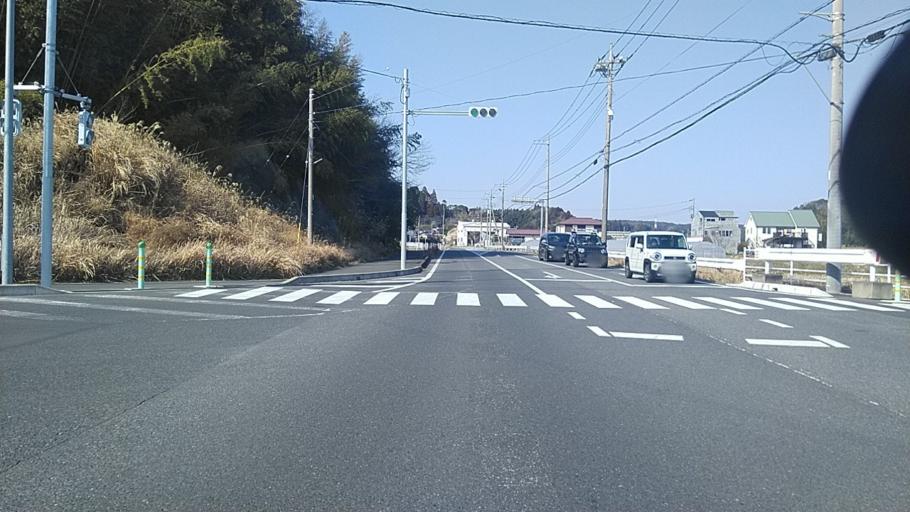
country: JP
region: Chiba
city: Oami
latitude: 35.4713
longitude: 140.2821
